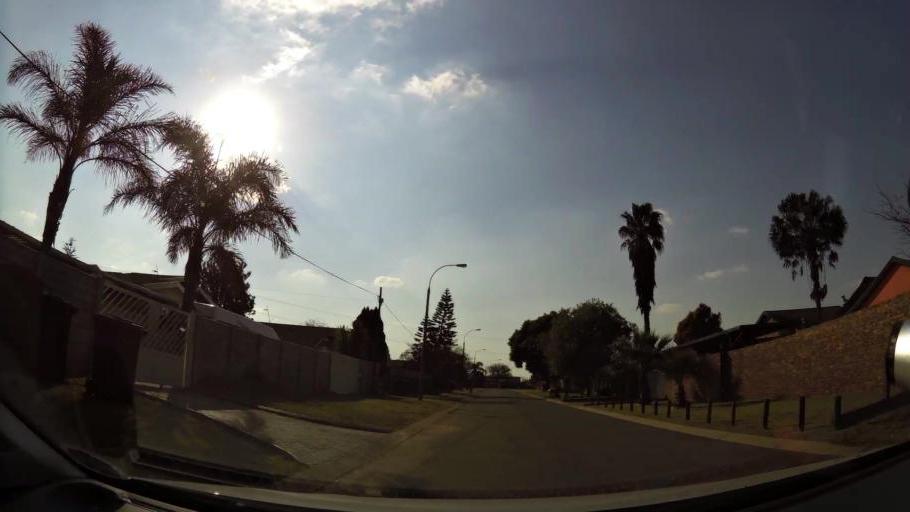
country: ZA
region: Gauteng
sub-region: City of Johannesburg Metropolitan Municipality
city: Modderfontein
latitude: -26.0814
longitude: 28.1905
